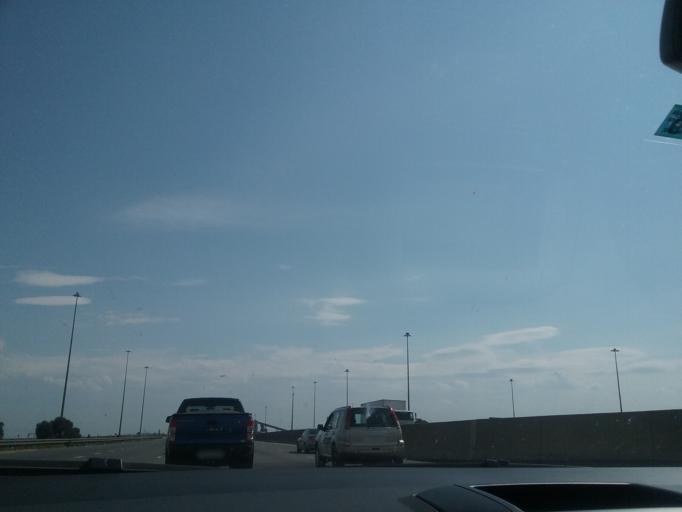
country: ZA
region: Gauteng
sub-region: Ekurhuleni Metropolitan Municipality
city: Germiston
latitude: -26.2124
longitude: 28.1345
